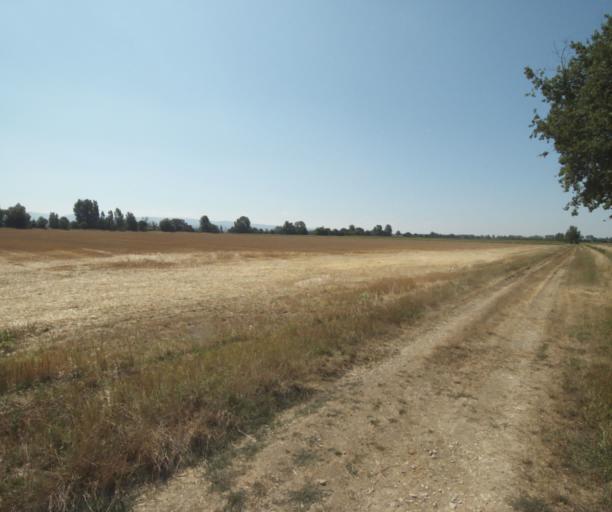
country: FR
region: Midi-Pyrenees
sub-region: Departement de la Haute-Garonne
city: Revel
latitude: 43.5159
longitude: 1.9648
